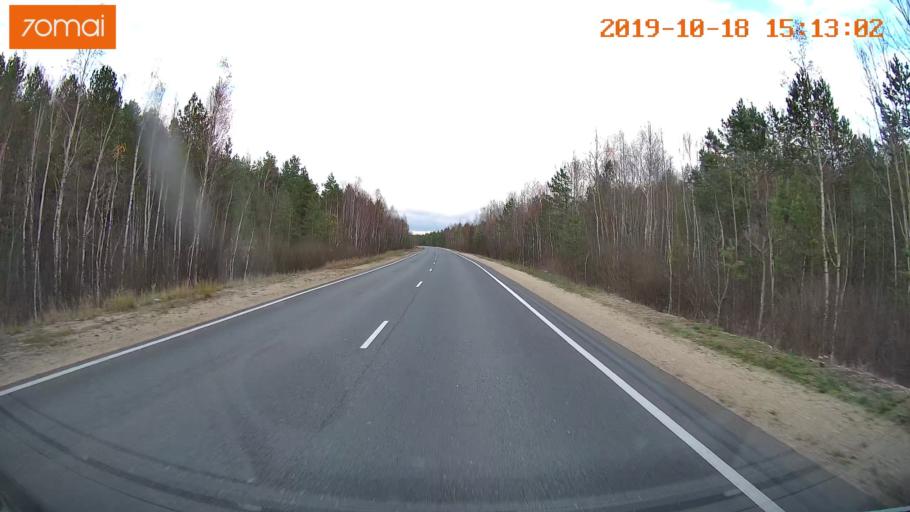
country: RU
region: Vladimir
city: Gus'-Khrustal'nyy
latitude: 55.5815
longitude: 40.7112
